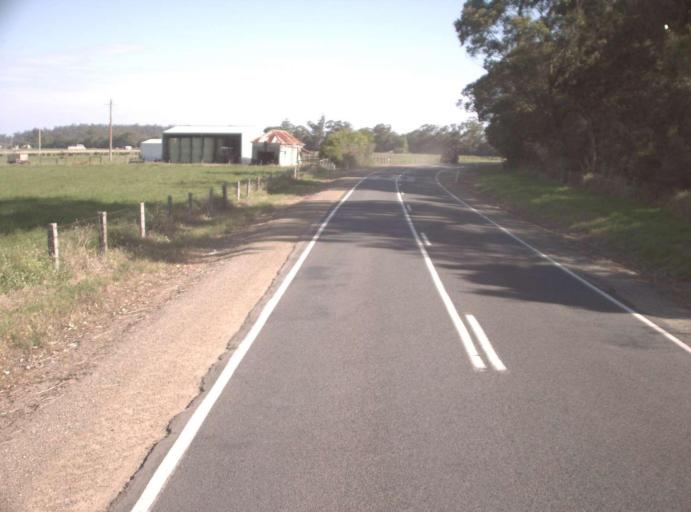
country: AU
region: Victoria
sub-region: East Gippsland
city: Lakes Entrance
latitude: -37.7326
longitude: 148.5048
